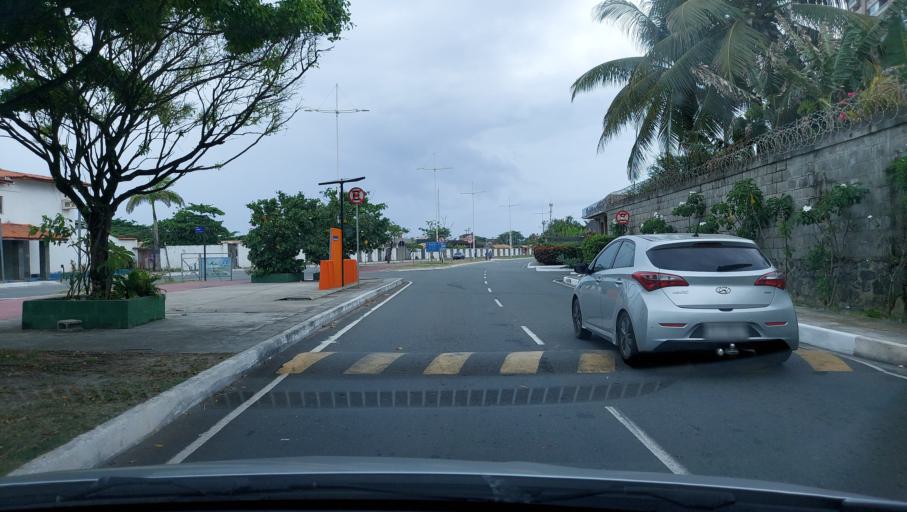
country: BR
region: Bahia
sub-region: Lauro De Freitas
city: Lauro de Freitas
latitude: -12.9591
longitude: -38.4018
